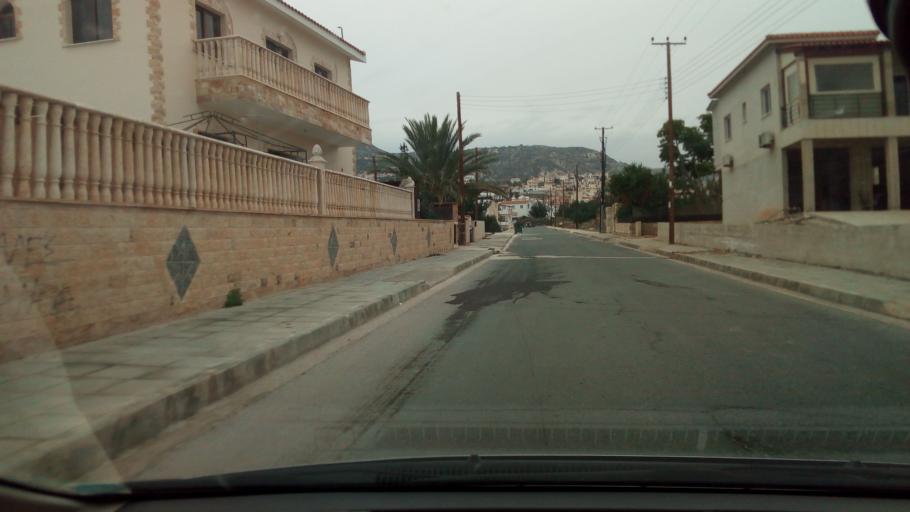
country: CY
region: Pafos
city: Pegeia
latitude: 34.8765
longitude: 32.3841
